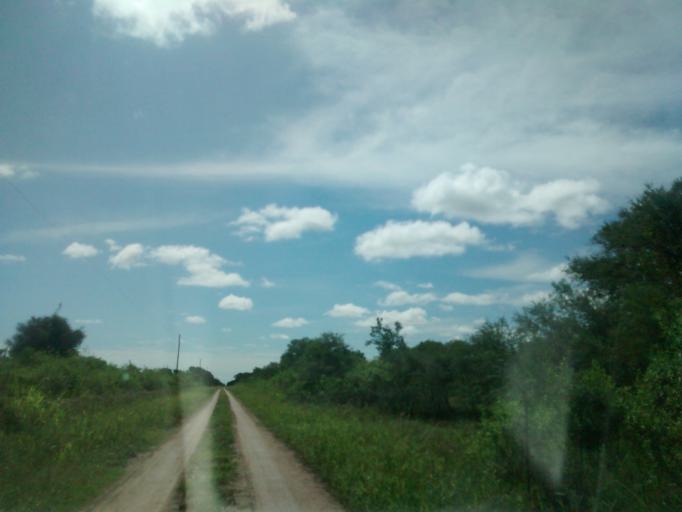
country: AR
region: Chaco
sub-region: Departamento de Quitilipi
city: Quitilipi
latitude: -26.7653
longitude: -60.2749
